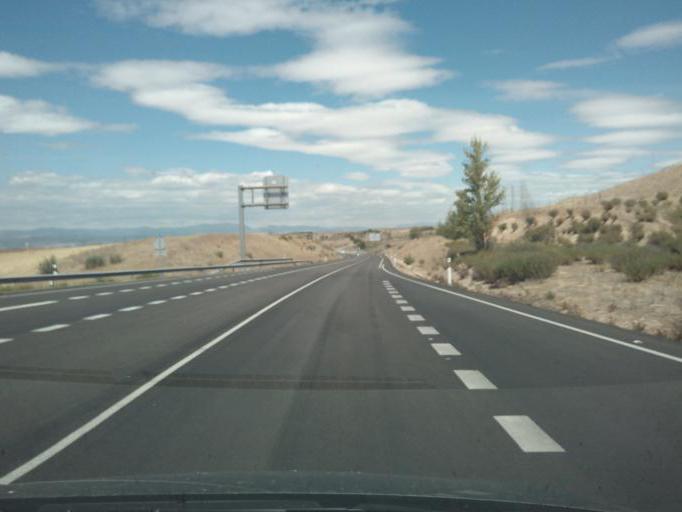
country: ES
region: Madrid
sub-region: Provincia de Madrid
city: Cobena
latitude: 40.5614
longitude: -3.5165
